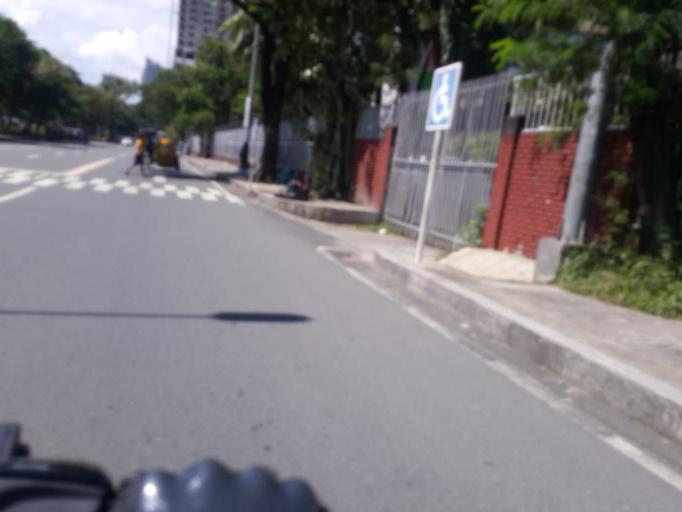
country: PH
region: Metro Manila
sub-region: City of Manila
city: Port Area
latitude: 14.5629
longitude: 120.9860
